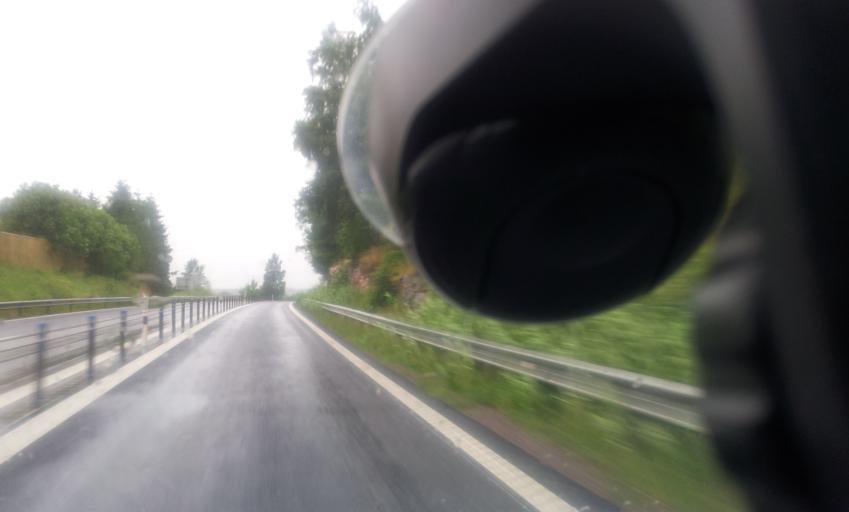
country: SE
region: OEstergoetland
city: Lindo
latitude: 58.5523
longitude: 16.2448
